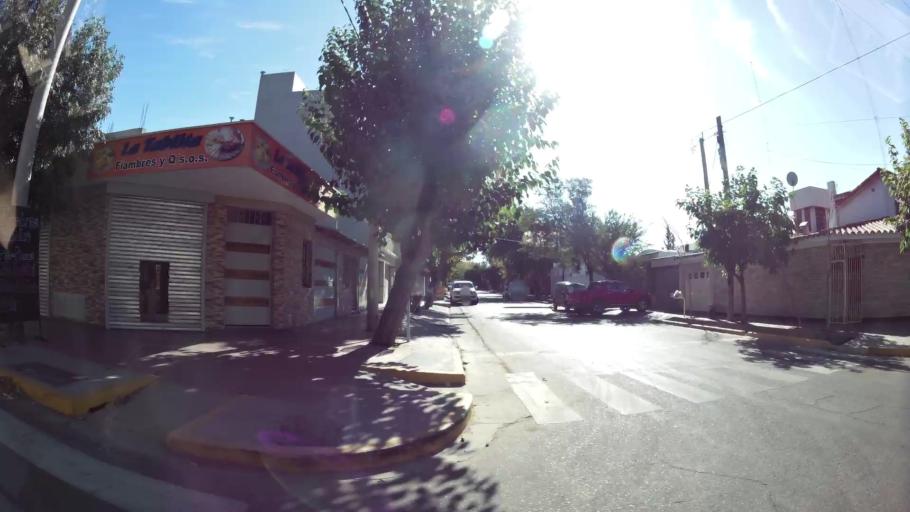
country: AR
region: Mendoza
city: Mendoza
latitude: -32.9020
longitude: -68.8328
